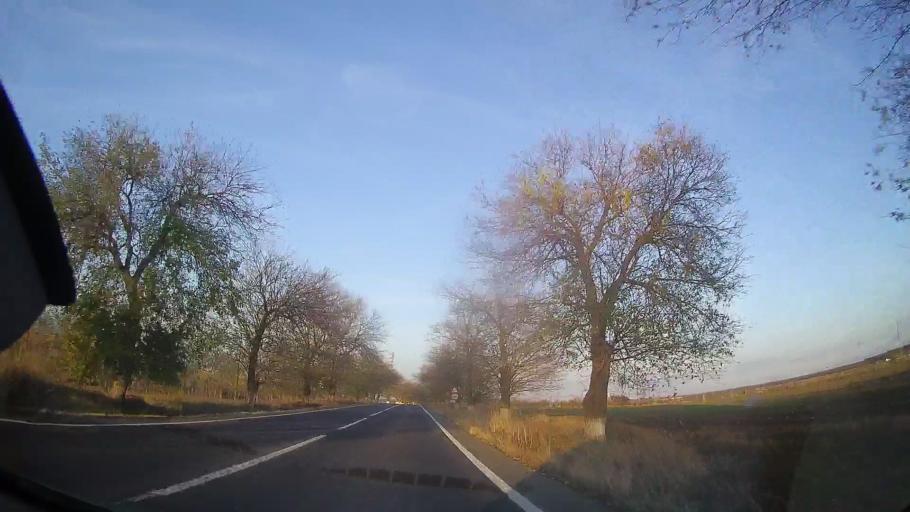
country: RO
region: Constanta
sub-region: Comuna Amzacea
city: Amzacea
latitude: 43.9541
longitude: 28.3861
